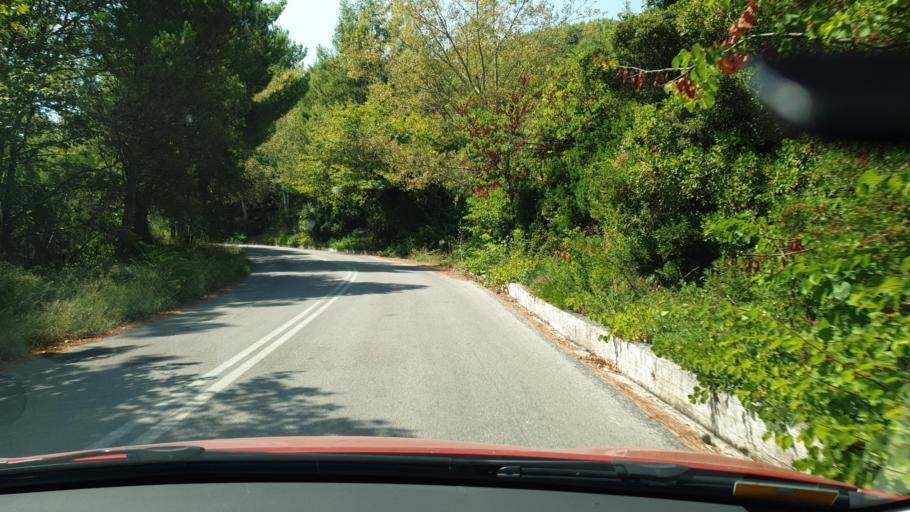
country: GR
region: Central Greece
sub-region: Nomos Evvoias
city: Kymi
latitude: 38.6281
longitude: 24.1004
